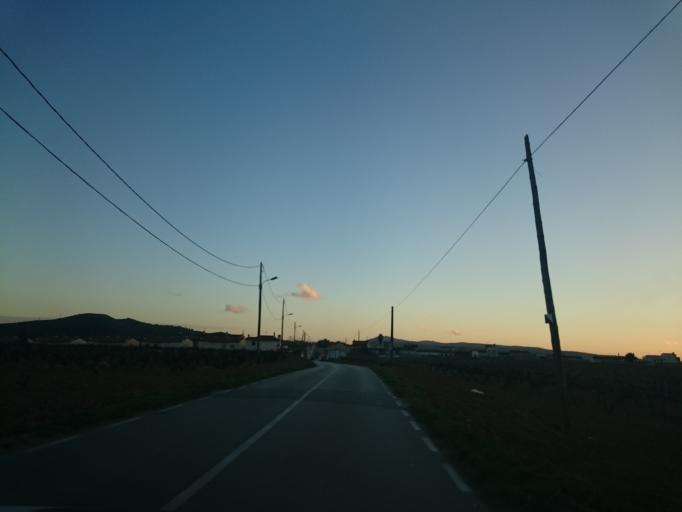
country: ES
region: Catalonia
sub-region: Provincia de Barcelona
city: La Granada
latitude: 41.3516
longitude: 1.7394
